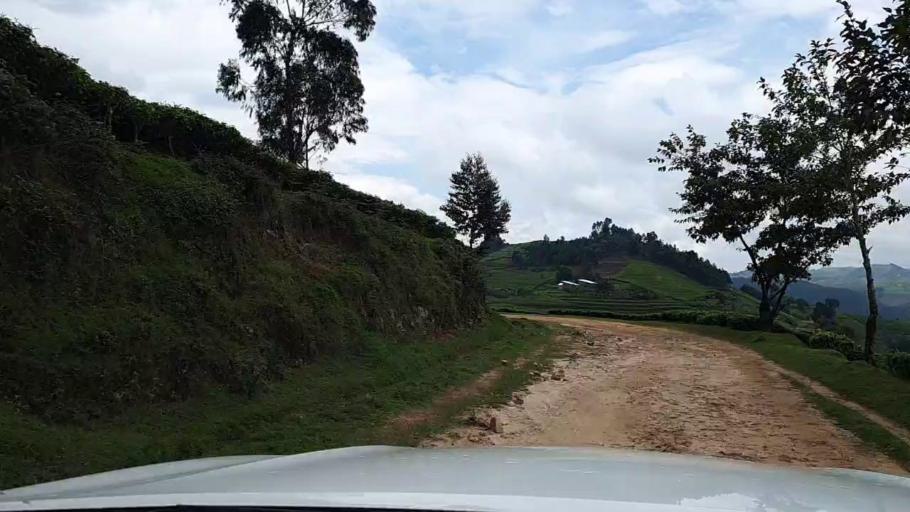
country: RW
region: Western Province
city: Kibuye
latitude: -2.2895
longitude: 29.3705
